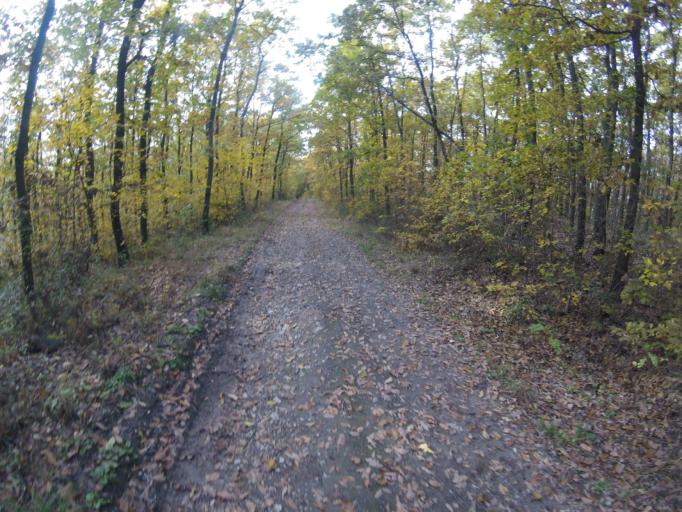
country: HU
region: Borsod-Abauj-Zemplen
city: Putnok
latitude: 48.2356
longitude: 20.4391
